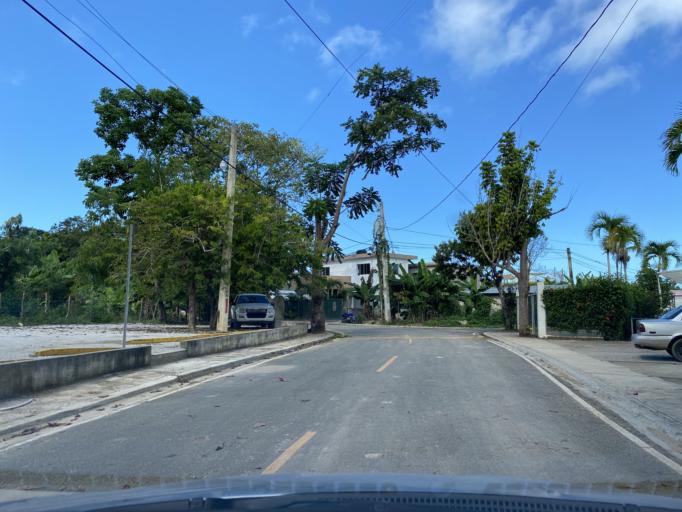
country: DO
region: Samana
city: Las Terrenas
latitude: 19.3028
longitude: -69.5408
